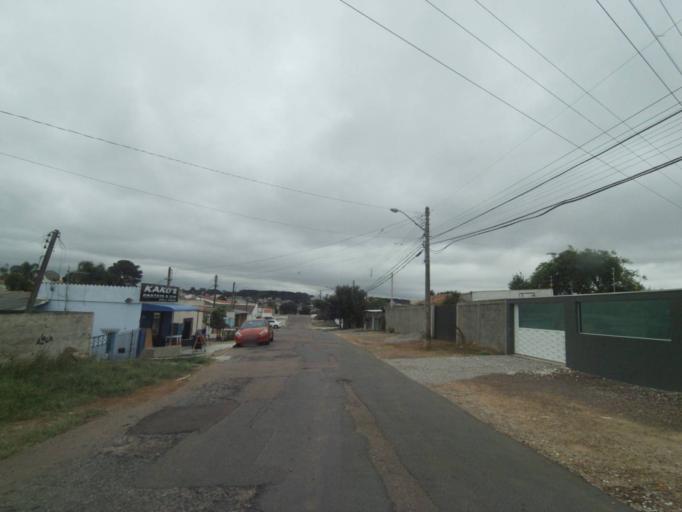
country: BR
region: Parana
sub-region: Sao Jose Dos Pinhais
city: Sao Jose dos Pinhais
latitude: -25.5449
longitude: -49.2887
